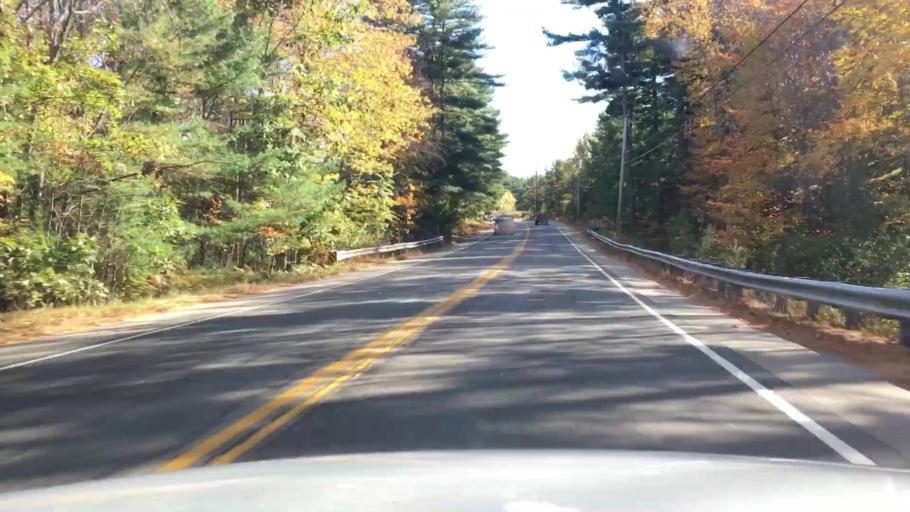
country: US
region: Maine
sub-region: York County
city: South Sanford
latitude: 43.3837
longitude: -70.6888
